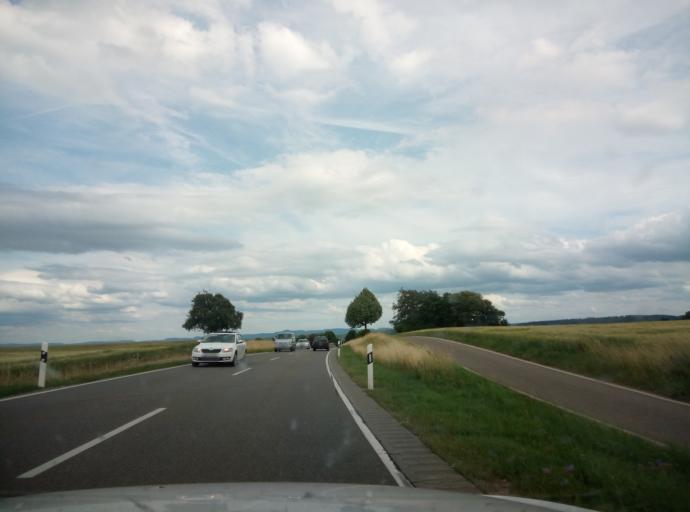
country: DE
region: Baden-Wuerttemberg
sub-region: Tuebingen Region
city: Rottenburg
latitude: 48.4893
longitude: 8.9224
